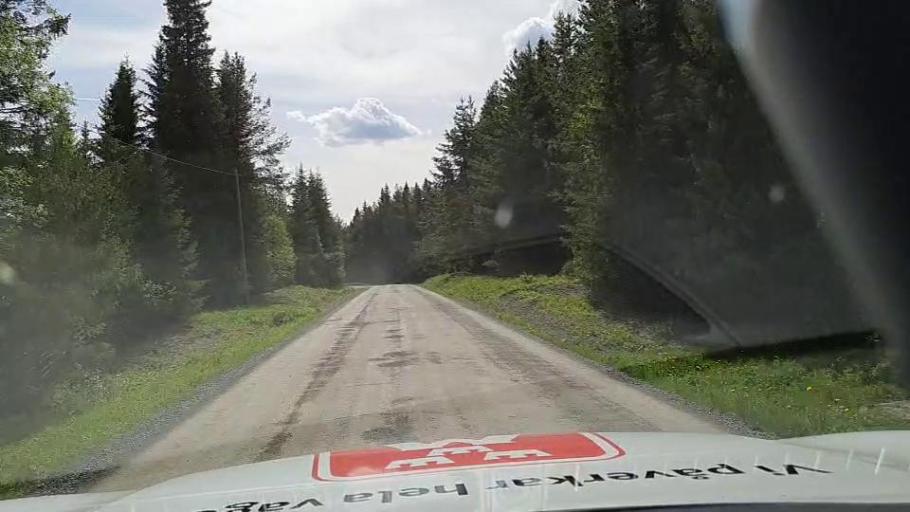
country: SE
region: Jaemtland
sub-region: OEstersunds Kommun
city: Brunflo
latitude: 63.0207
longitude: 14.7730
